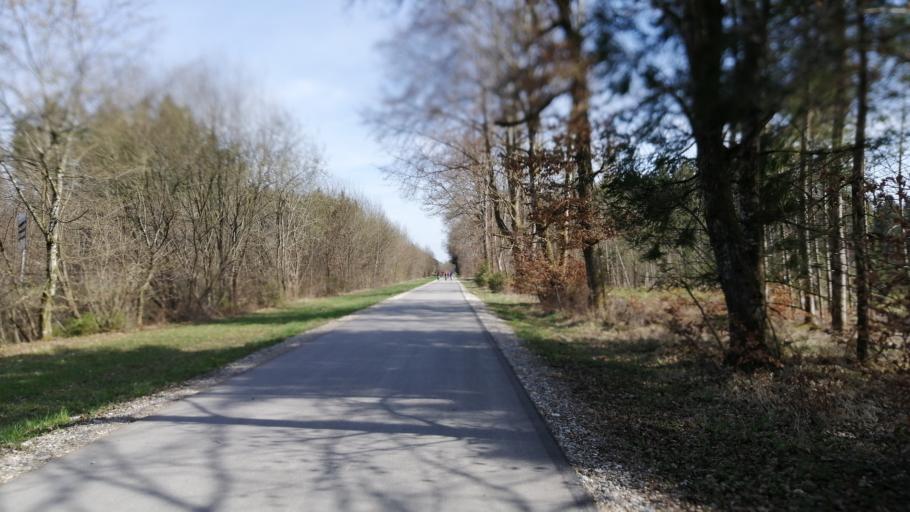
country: DE
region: Bavaria
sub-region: Upper Bavaria
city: Oberhaching
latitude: 48.0053
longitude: 11.5978
